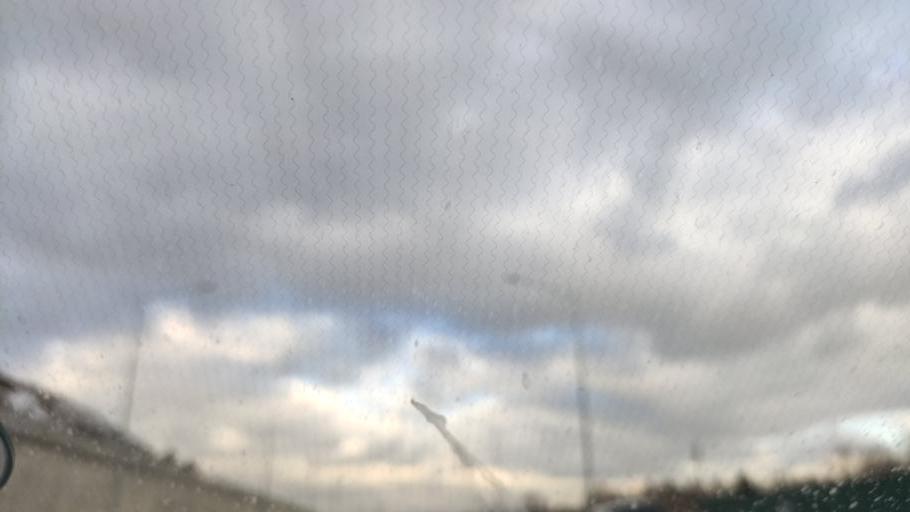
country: RU
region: Moskovskaya
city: Mosrentgen
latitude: 55.6119
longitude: 37.4358
